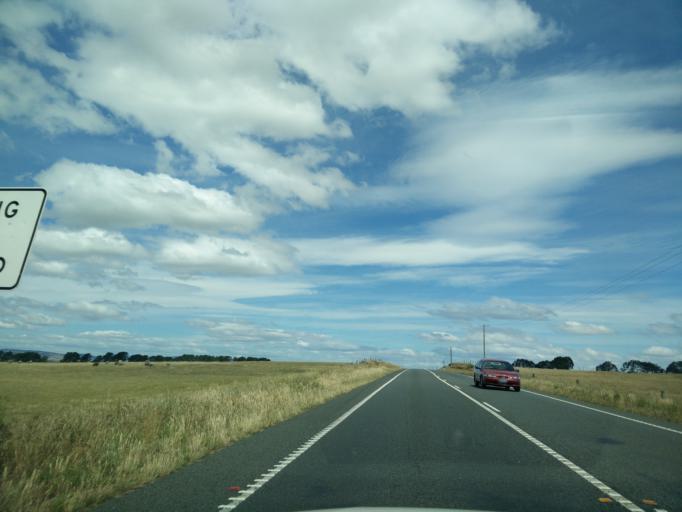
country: AU
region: Tasmania
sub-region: Northern Midlands
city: Evandale
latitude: -41.7055
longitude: 147.2967
